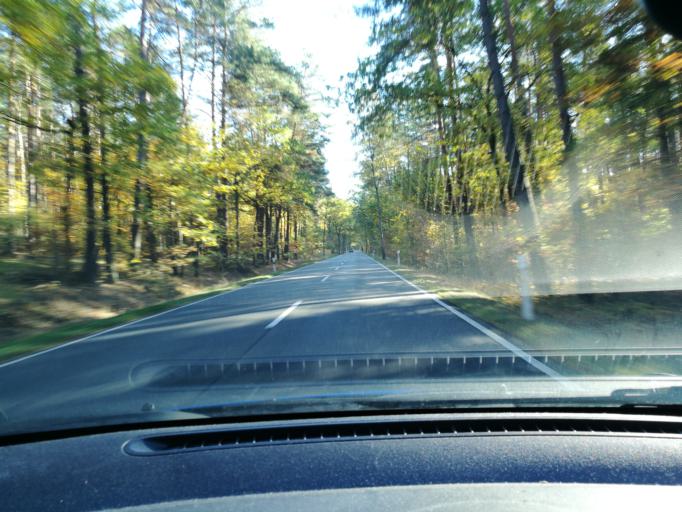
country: DE
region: Lower Saxony
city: Karwitz
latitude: 53.1216
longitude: 10.9846
